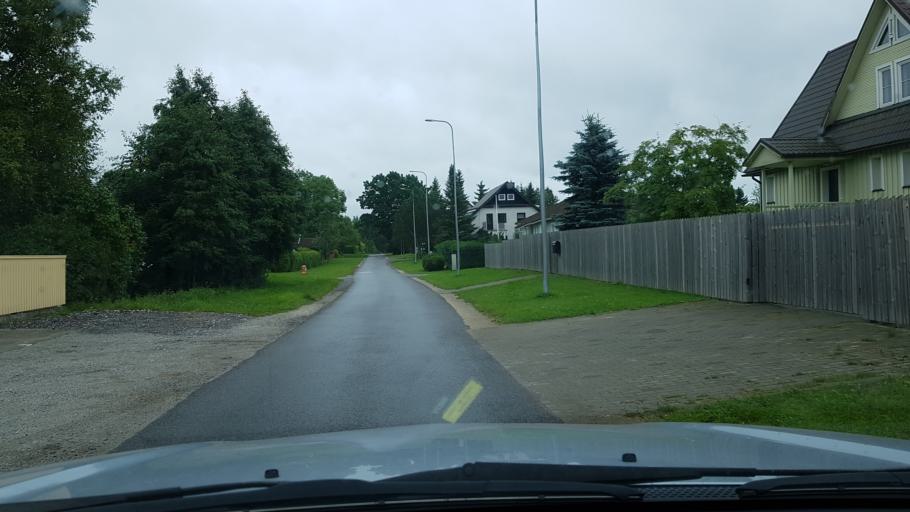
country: EE
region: Harju
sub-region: Rae vald
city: Jueri
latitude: 59.3549
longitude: 24.9187
